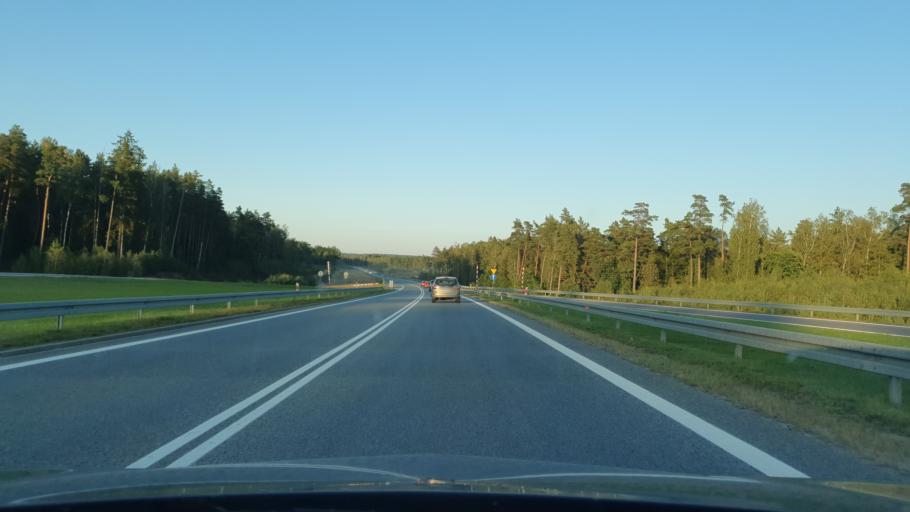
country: PL
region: Pomeranian Voivodeship
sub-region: Slupsk
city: Slupsk
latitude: 54.4328
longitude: 17.0598
